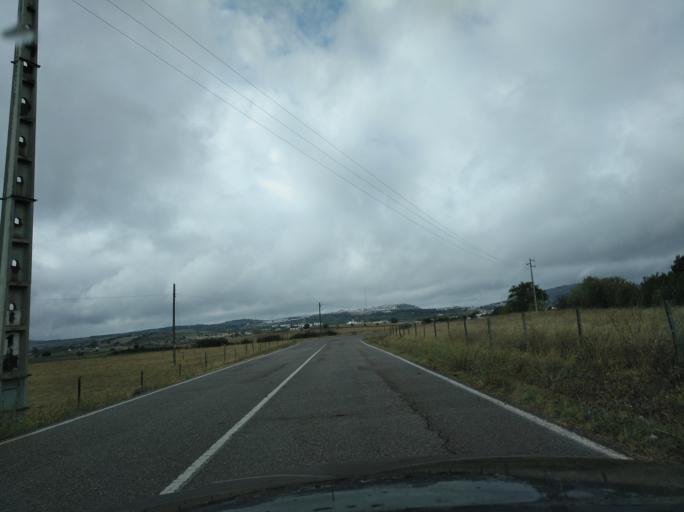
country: PT
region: Portalegre
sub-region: Elvas
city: Elvas
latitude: 38.8880
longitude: -7.1165
